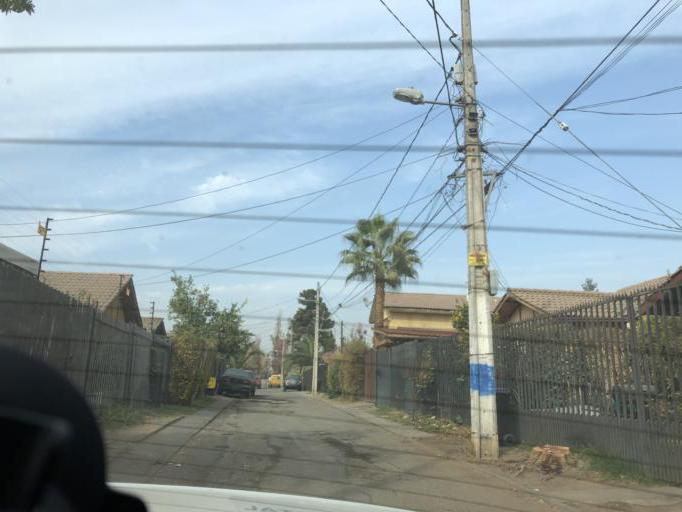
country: CL
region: Santiago Metropolitan
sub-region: Provincia de Cordillera
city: Puente Alto
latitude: -33.5509
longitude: -70.5567
